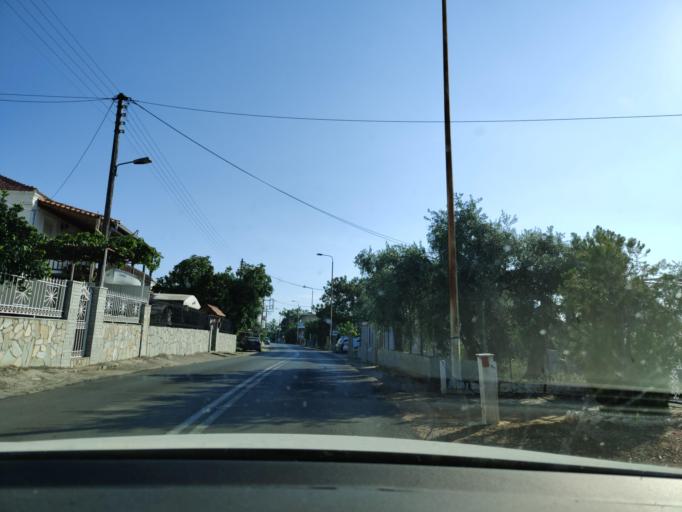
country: GR
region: East Macedonia and Thrace
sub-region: Nomos Kavalas
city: Prinos
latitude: 40.7030
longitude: 24.5303
